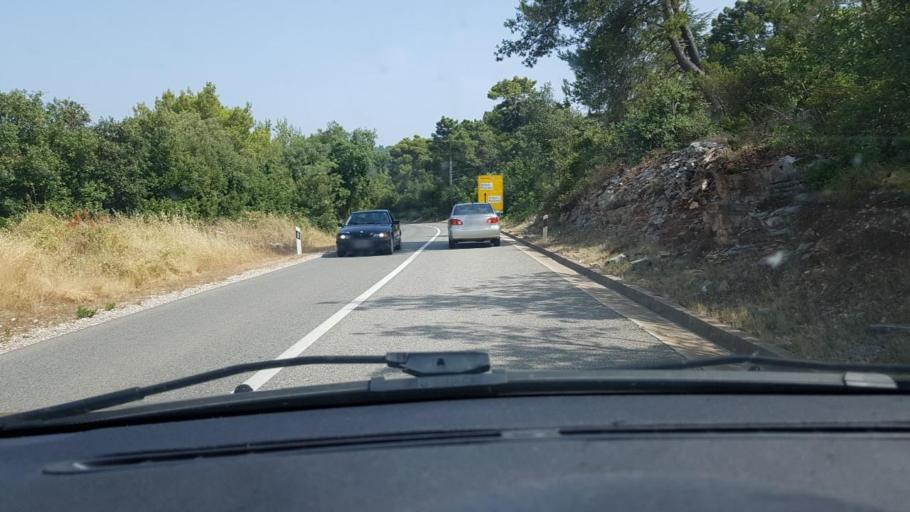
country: HR
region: Dubrovacko-Neretvanska
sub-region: Grad Korcula
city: Zrnovo
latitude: 42.9360
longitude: 17.0997
